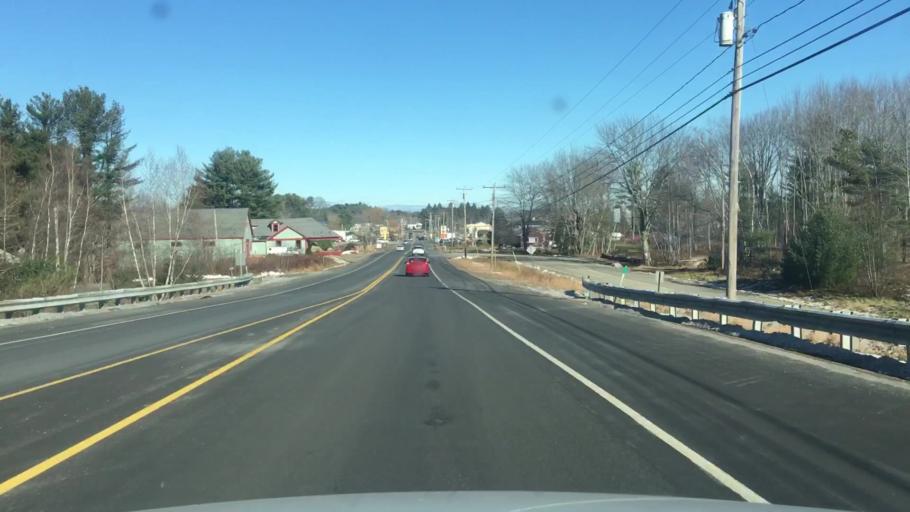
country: US
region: Maine
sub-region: York County
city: Biddeford
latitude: 43.4574
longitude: -70.4932
